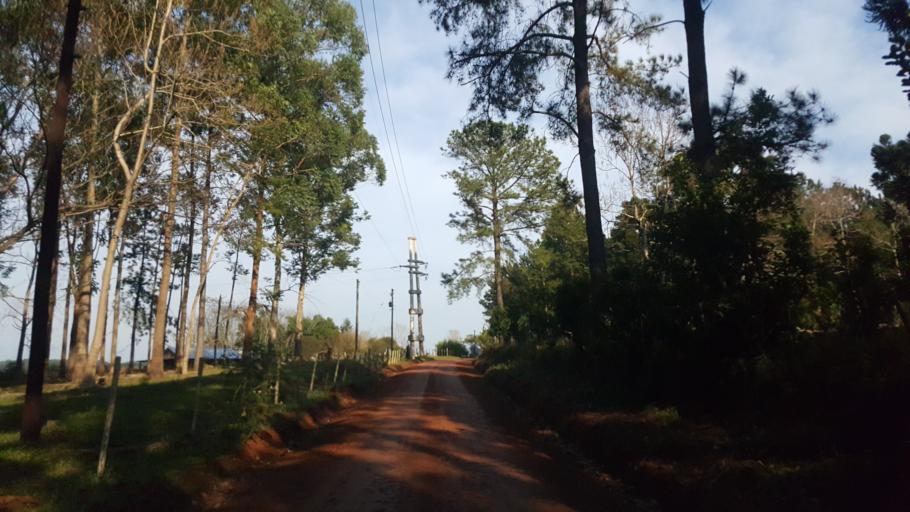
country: AR
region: Misiones
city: Capiovi
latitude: -26.9149
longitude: -55.0710
